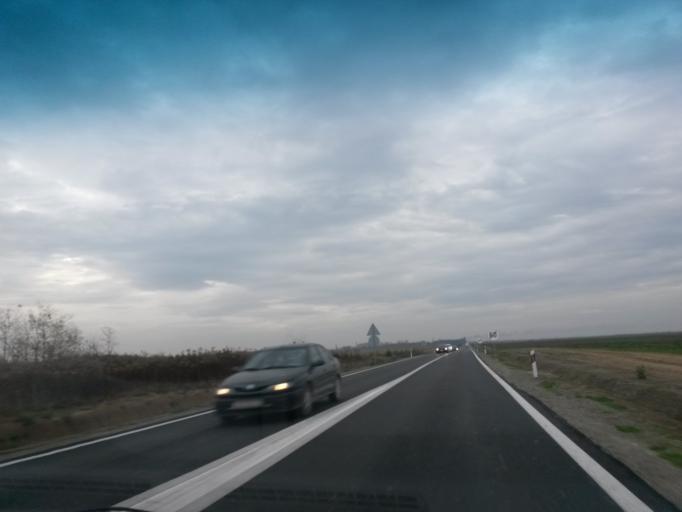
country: HR
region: Osjecko-Baranjska
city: Tenja
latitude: 45.5108
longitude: 18.7914
